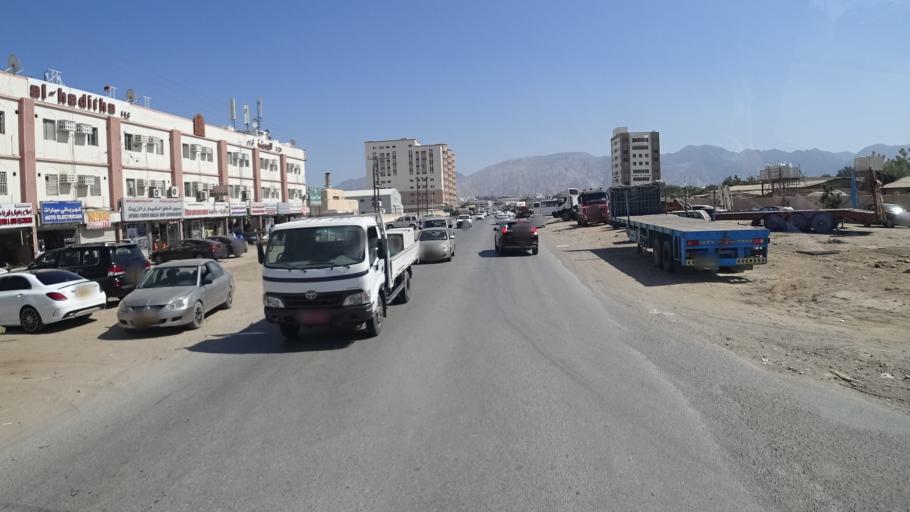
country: OM
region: Muhafazat Masqat
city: Bawshar
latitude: 23.5740
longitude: 58.3733
